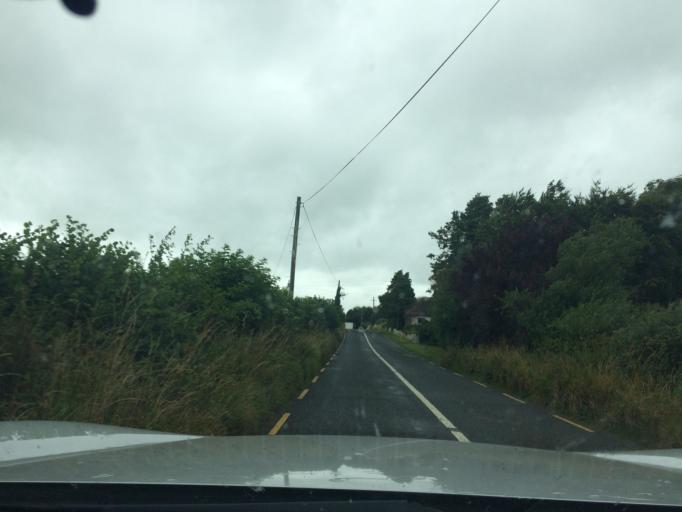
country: IE
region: Munster
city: Cashel
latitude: 52.6119
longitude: -7.8805
